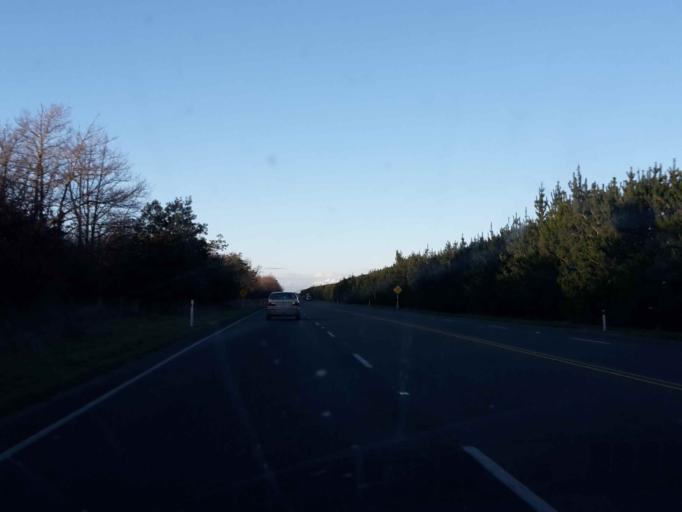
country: NZ
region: Canterbury
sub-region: Selwyn District
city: Burnham
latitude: -43.6313
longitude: 172.2724
